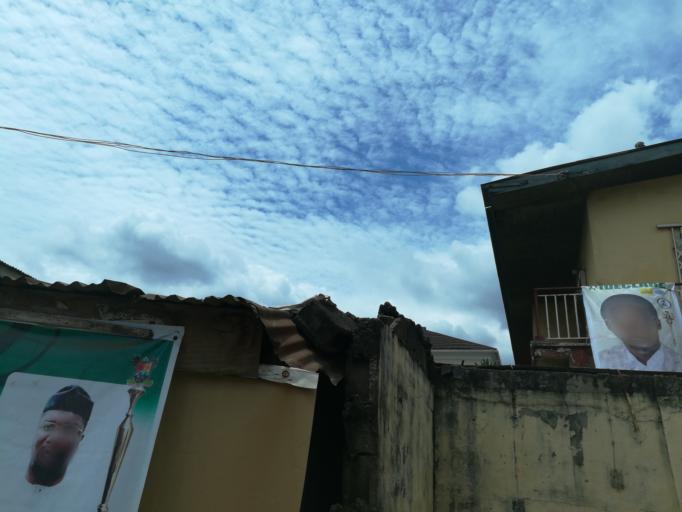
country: NG
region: Lagos
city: Oshodi
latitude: 6.5643
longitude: 3.3314
